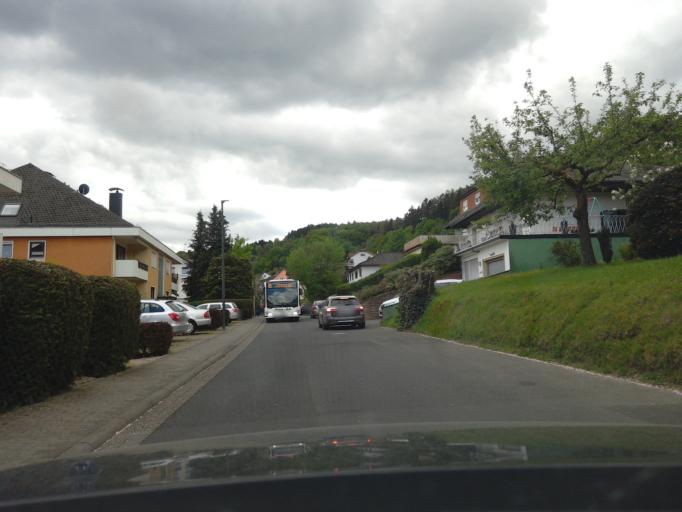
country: DE
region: Hesse
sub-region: Regierungsbezirk Darmstadt
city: Bad Orb
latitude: 50.2194
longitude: 9.3468
